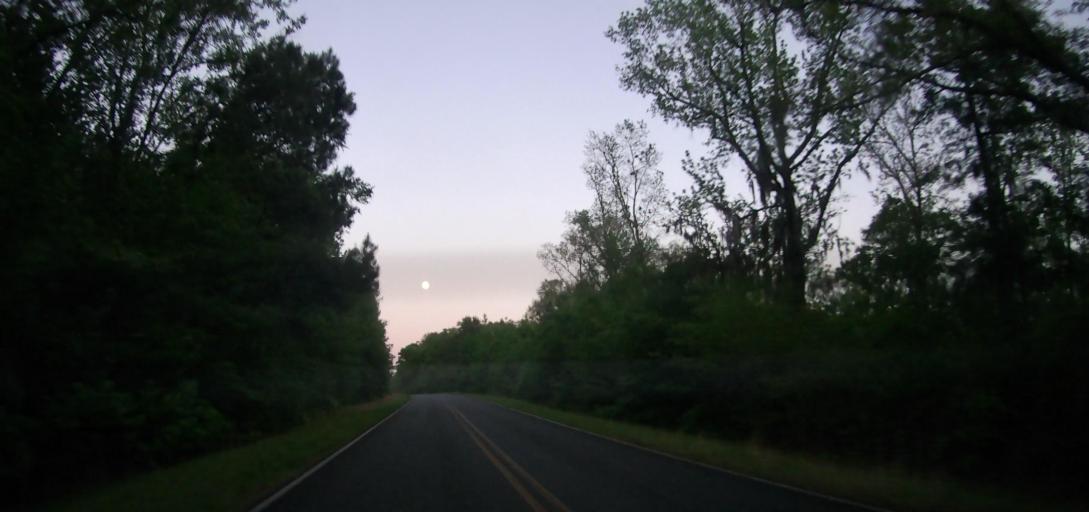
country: US
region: Georgia
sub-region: Marion County
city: Buena Vista
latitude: 32.2556
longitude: -84.6275
